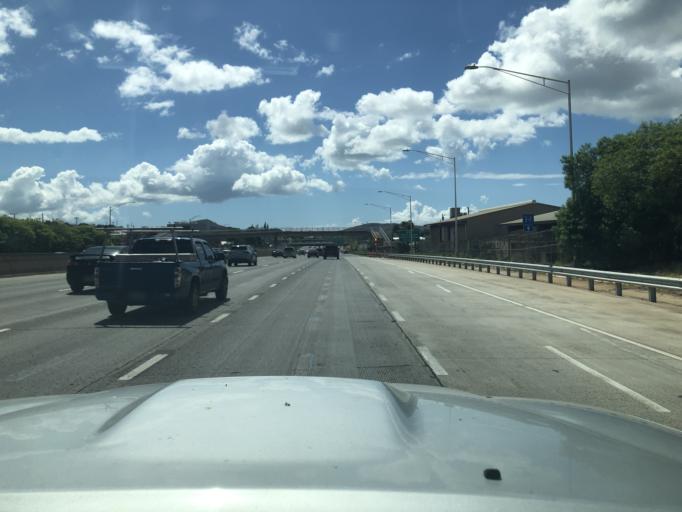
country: US
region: Hawaii
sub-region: Honolulu County
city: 'Aiea
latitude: 21.3837
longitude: -157.9321
